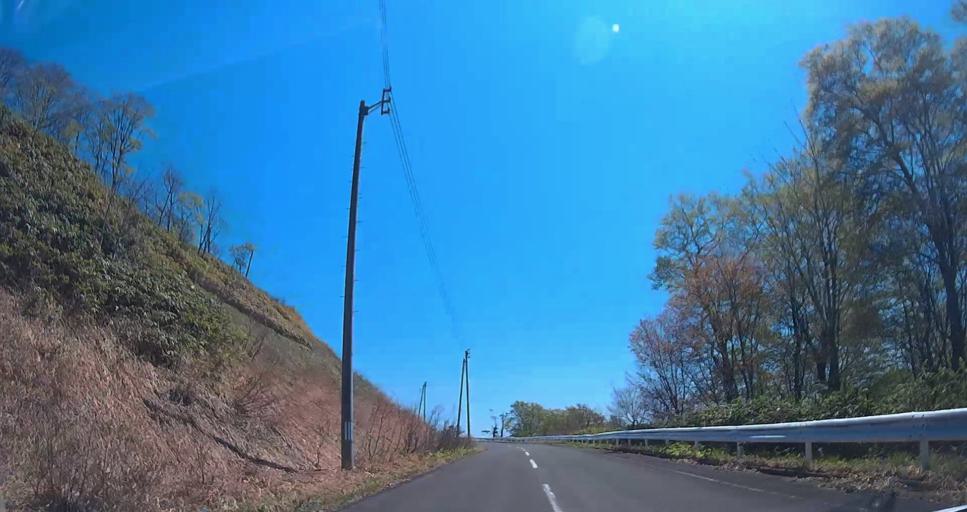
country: JP
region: Aomori
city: Mutsu
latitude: 41.2323
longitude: 140.8169
